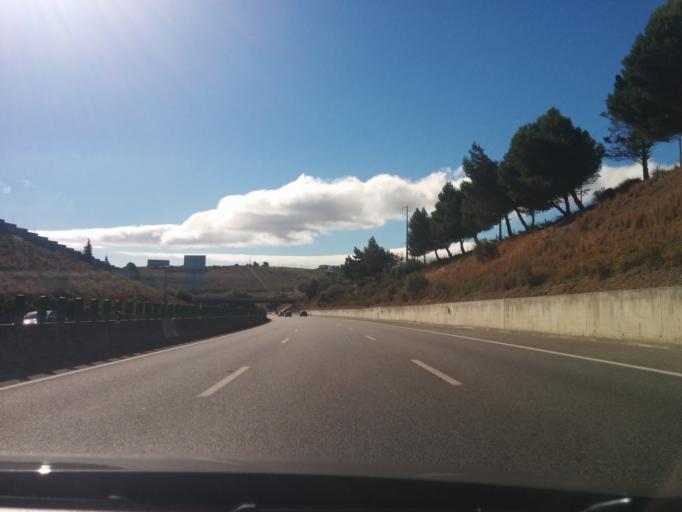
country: PT
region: Lisbon
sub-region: Cascais
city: Parede
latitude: 38.7179
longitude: -9.3617
